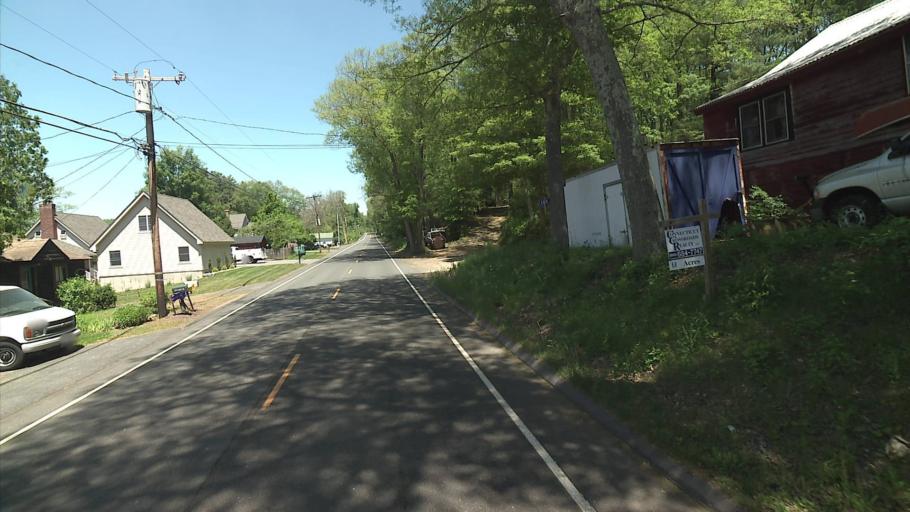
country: US
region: Connecticut
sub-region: Tolland County
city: Stafford
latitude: 42.0129
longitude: -72.2536
